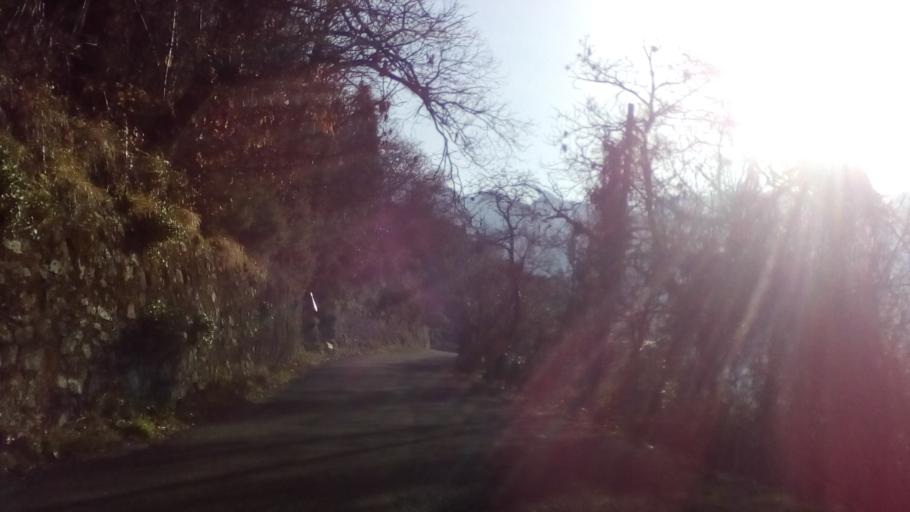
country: IT
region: Tuscany
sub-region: Provincia di Massa-Carrara
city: Montignoso
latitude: 44.0574
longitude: 10.1861
